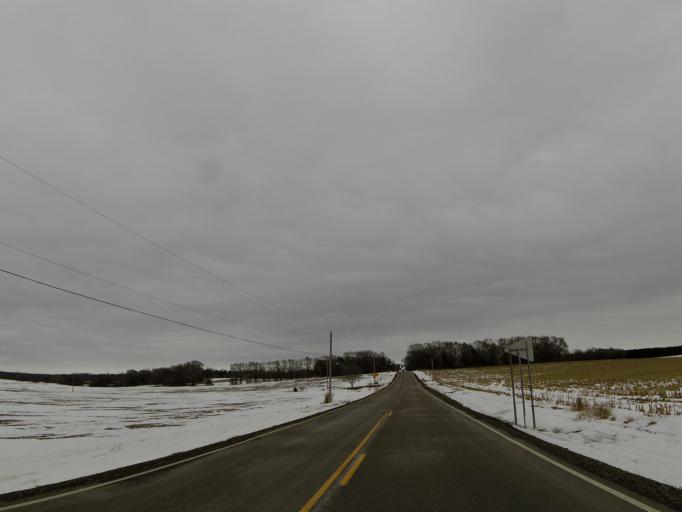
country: US
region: Wisconsin
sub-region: Pierce County
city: Prescott
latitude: 44.8189
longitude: -92.8337
